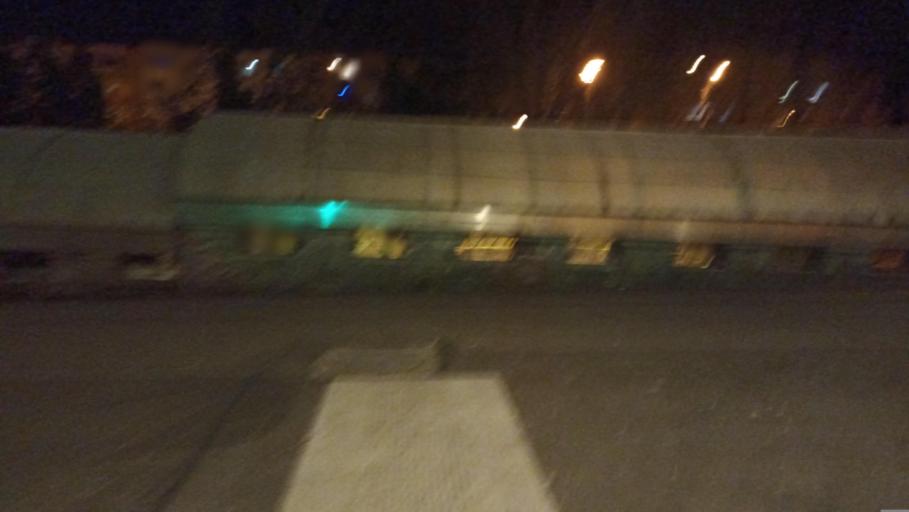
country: RO
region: Cluj
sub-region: Municipiul Cluj-Napoca
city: Cluj-Napoca
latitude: 46.7538
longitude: 23.5509
